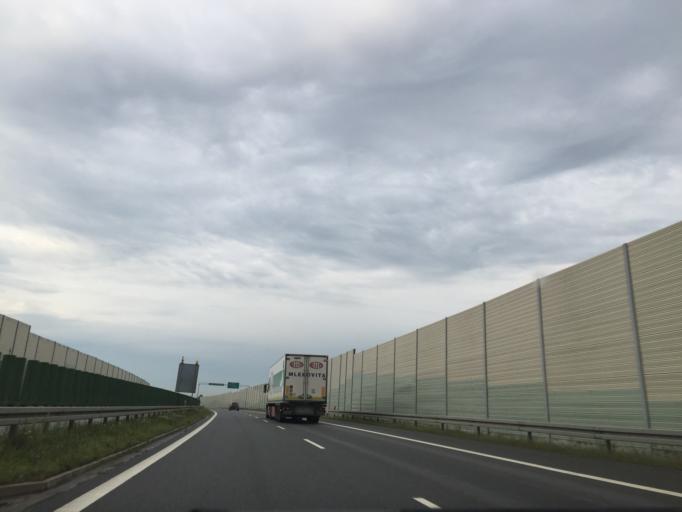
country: PL
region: Podlasie
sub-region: Powiat zambrowski
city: Zambrow
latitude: 52.9666
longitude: 22.2041
